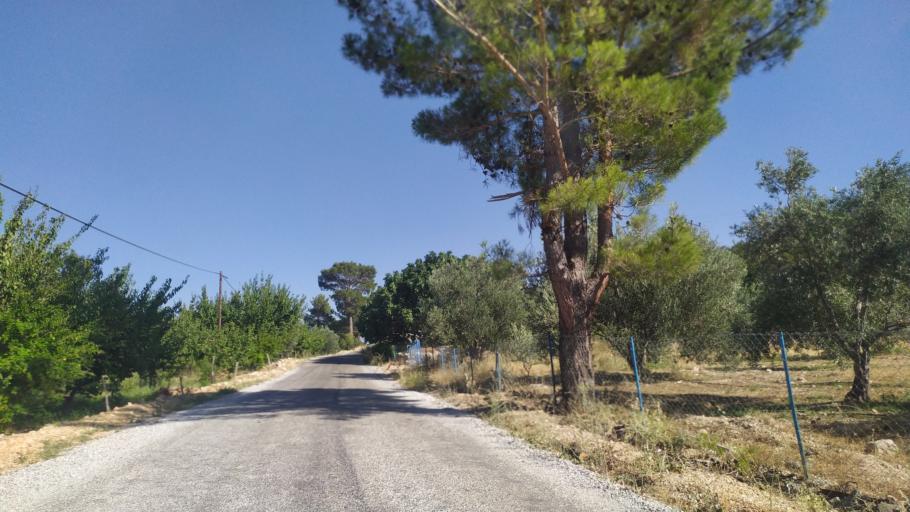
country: TR
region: Mersin
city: Mut
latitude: 36.7016
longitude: 33.4777
